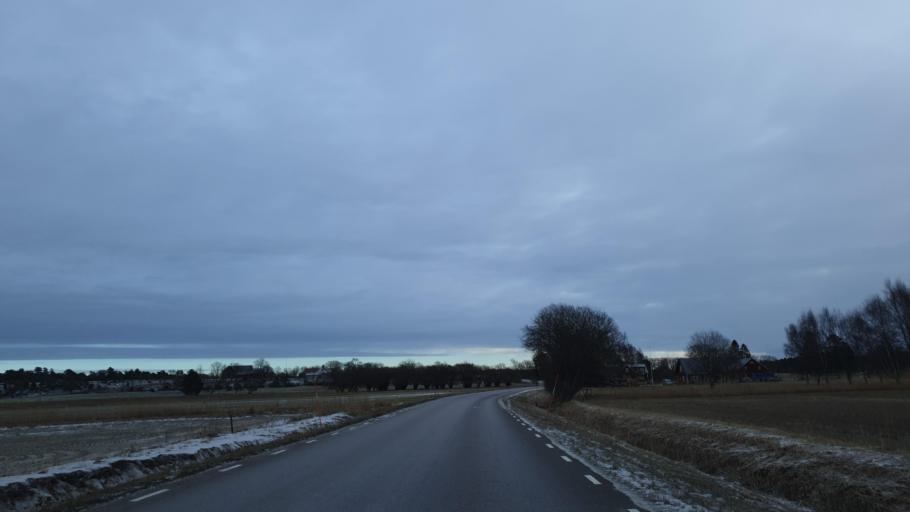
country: SE
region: Gotland
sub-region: Gotland
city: Slite
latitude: 57.4192
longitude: 18.8728
